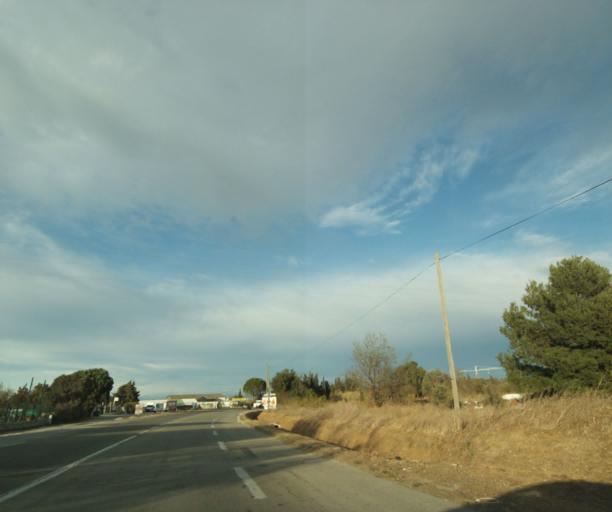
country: FR
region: Provence-Alpes-Cote d'Azur
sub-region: Departement des Bouches-du-Rhone
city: Chateauneuf-les-Martigues
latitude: 43.3768
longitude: 5.1866
